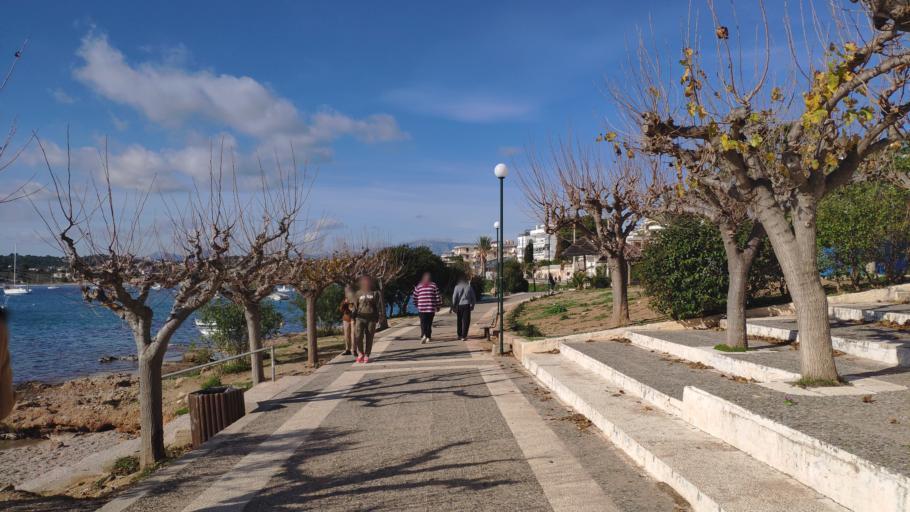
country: GR
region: Attica
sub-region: Nomarchia Anatolikis Attikis
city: Limin Mesoyaias
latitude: 37.8927
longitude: 24.0185
